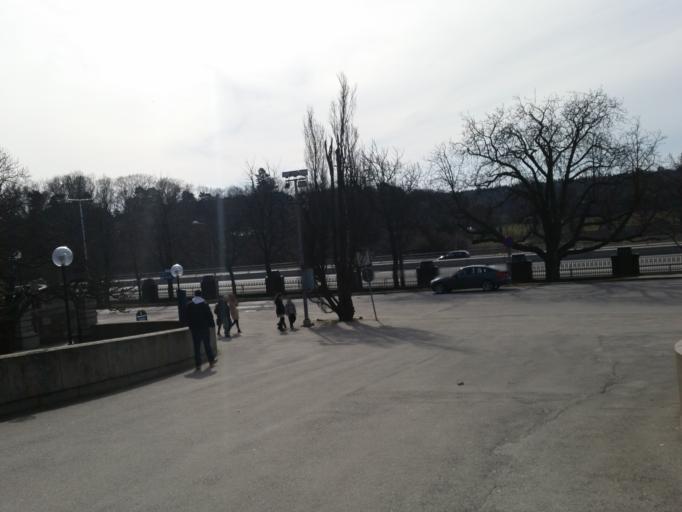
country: SE
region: Stockholm
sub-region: Norrtalje Kommun
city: Bergshamra
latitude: 59.3685
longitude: 18.0530
